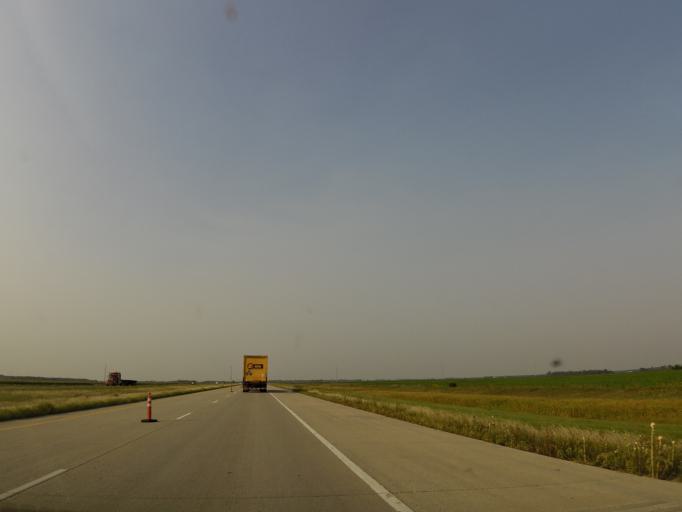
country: US
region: North Dakota
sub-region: Cass County
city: Horace
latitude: 46.6711
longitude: -96.8309
